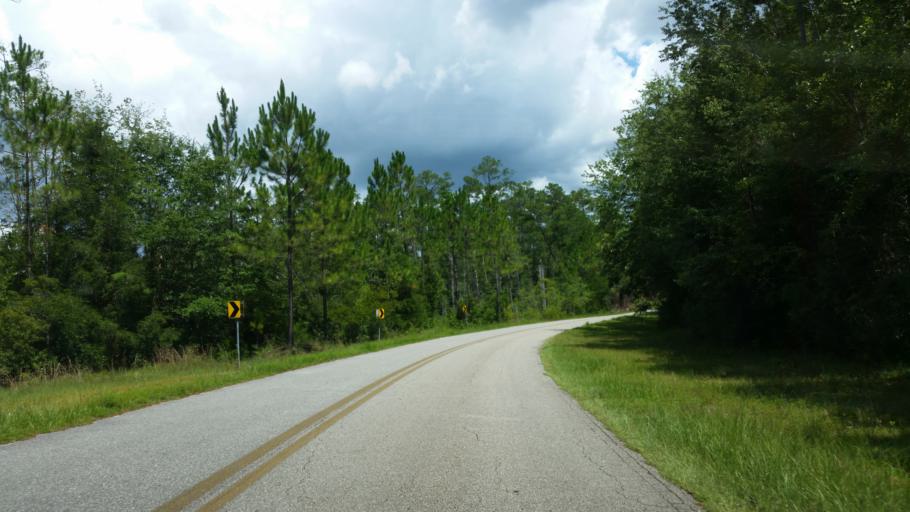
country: US
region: Florida
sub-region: Okaloosa County
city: Crestview
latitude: 30.7226
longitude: -86.7884
